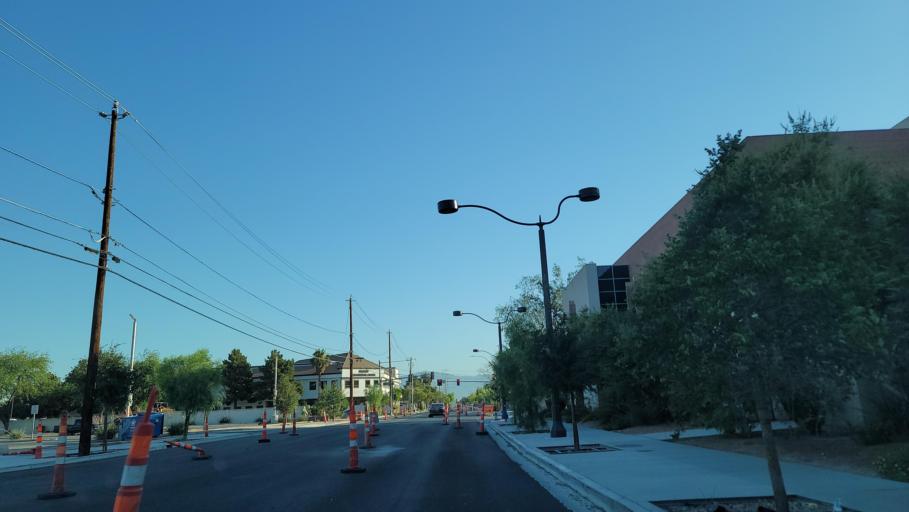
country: US
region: Nevada
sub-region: Clark County
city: Las Vegas
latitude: 36.1650
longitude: -115.1654
